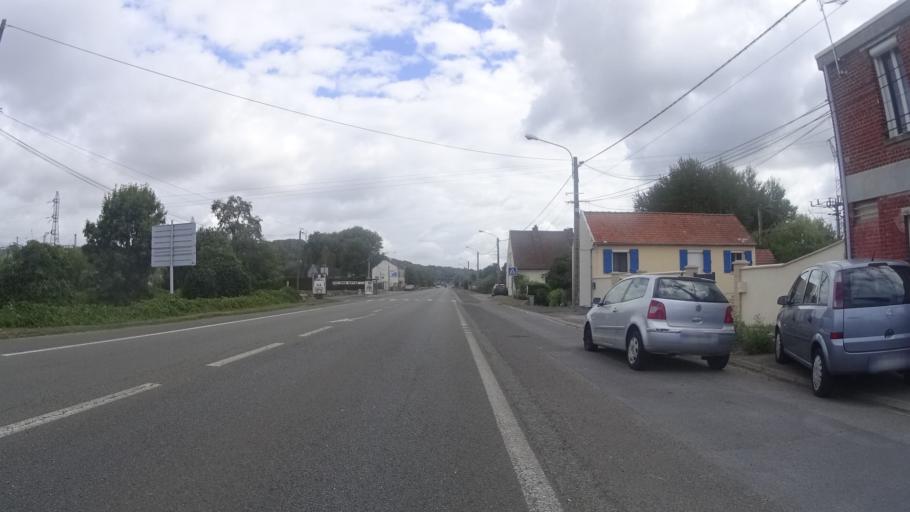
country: FR
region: Picardie
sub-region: Departement de l'Oise
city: Clairoix
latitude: 49.4334
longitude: 2.8414
